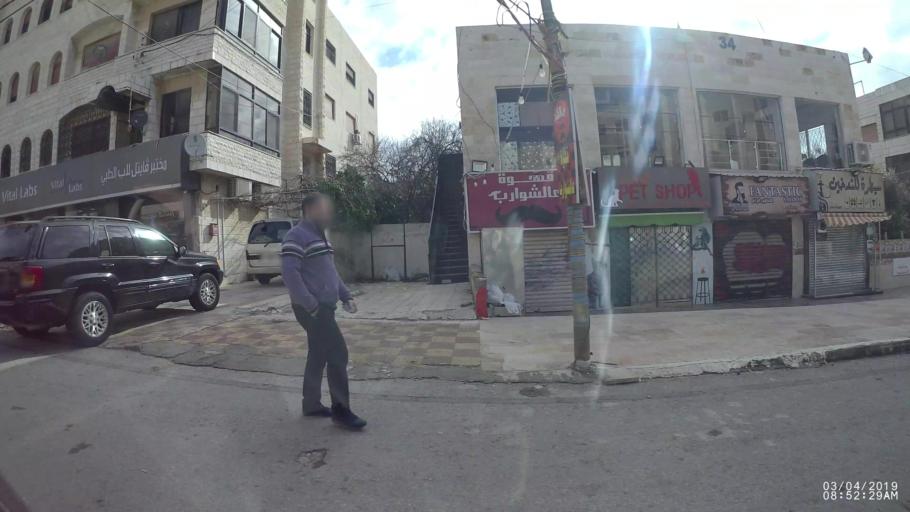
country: JO
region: Amman
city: Wadi as Sir
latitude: 31.9504
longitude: 35.8406
